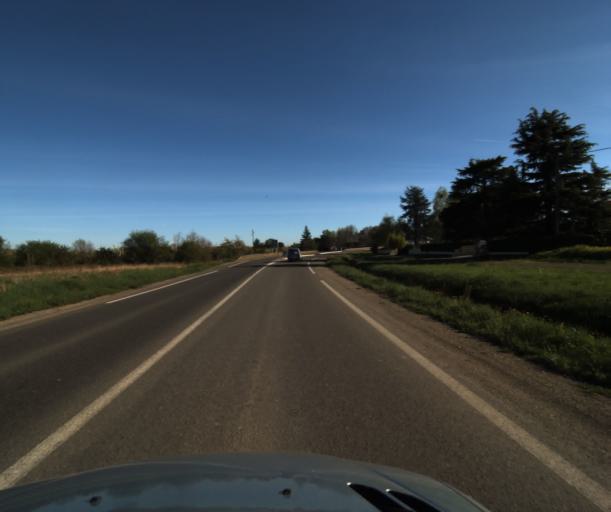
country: FR
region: Midi-Pyrenees
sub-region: Departement du Tarn-et-Garonne
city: Moissac
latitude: 44.1113
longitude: 1.1151
